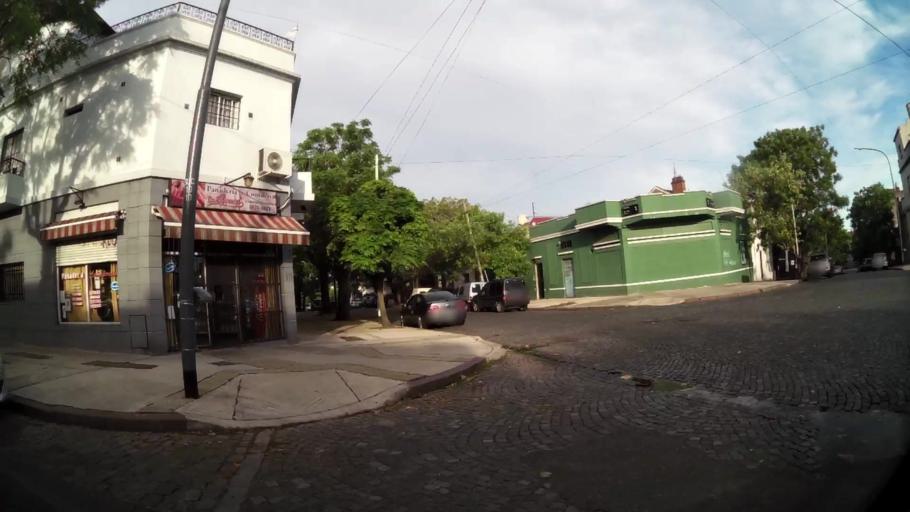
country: AR
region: Buenos Aires F.D.
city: Buenos Aires
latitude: -34.6420
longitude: -58.4271
